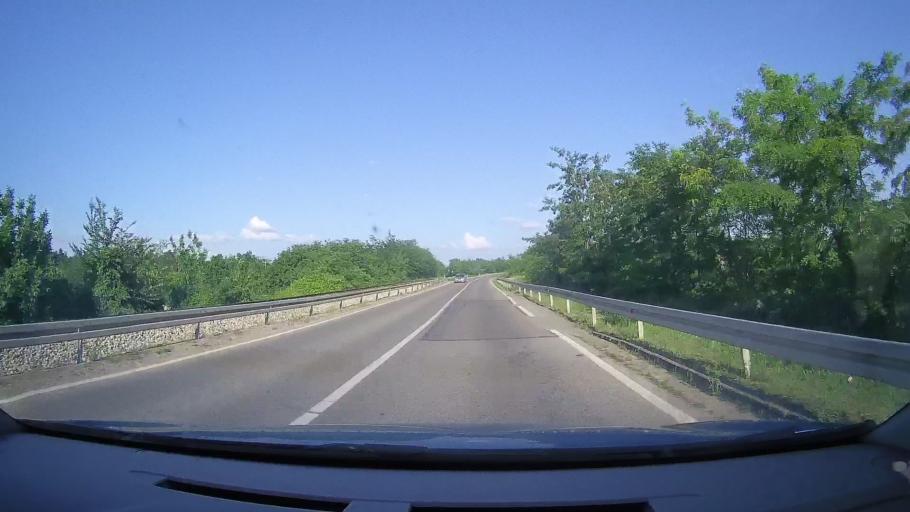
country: RS
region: Autonomna Pokrajina Vojvodina
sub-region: Juznobanatski Okrug
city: Alibunar
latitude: 45.0681
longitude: 20.9665
